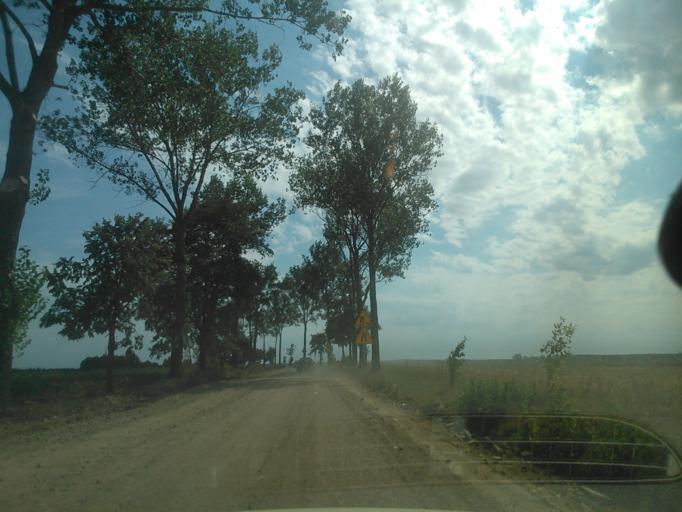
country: PL
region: Warmian-Masurian Voivodeship
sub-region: Powiat dzialdowski
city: Ilowo -Osada
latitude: 53.1935
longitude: 20.2717
